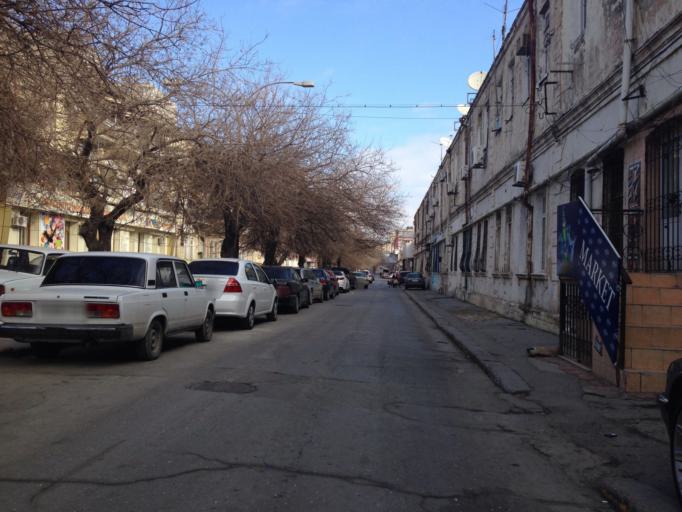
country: AZ
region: Baki
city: Baku
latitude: 40.3898
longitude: 49.8579
